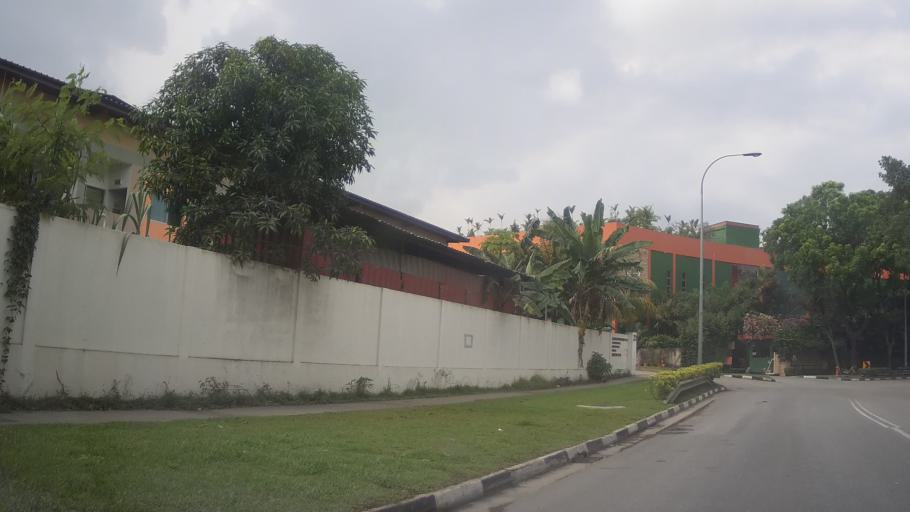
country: MY
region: Johor
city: Johor Bahru
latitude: 1.4332
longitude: 103.7507
